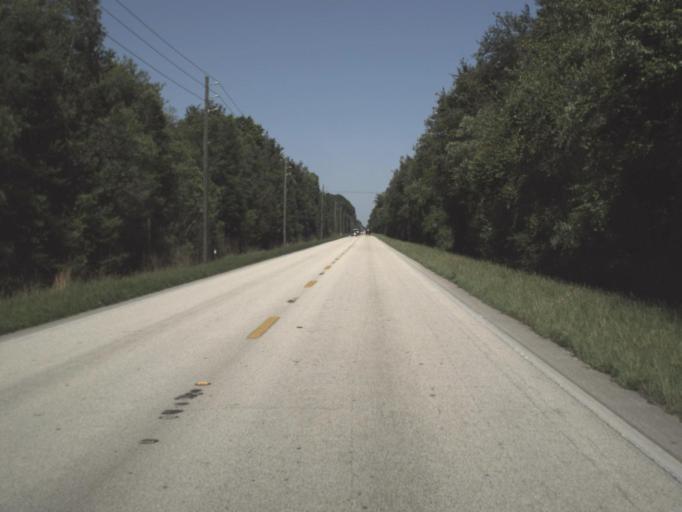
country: US
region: Florida
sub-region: Duval County
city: Baldwin
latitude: 30.3057
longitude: -81.9289
